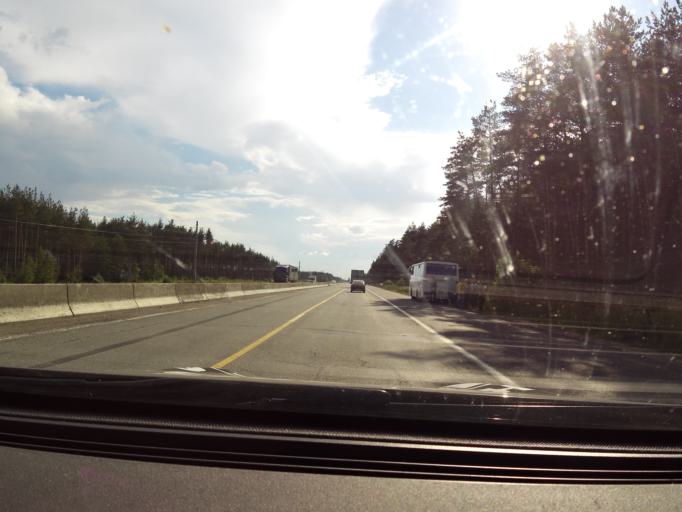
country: RU
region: Nizjnij Novgorod
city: Mulino
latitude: 56.2642
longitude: 42.9278
